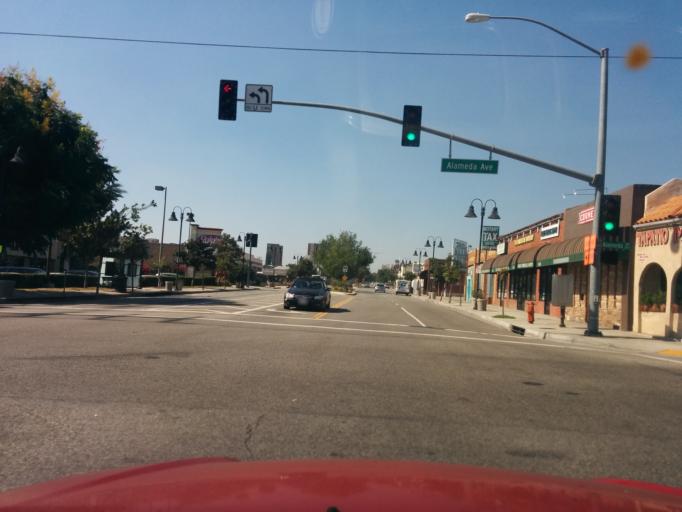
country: US
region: California
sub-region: Los Angeles County
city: Burbank
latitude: 34.1745
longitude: -118.2998
